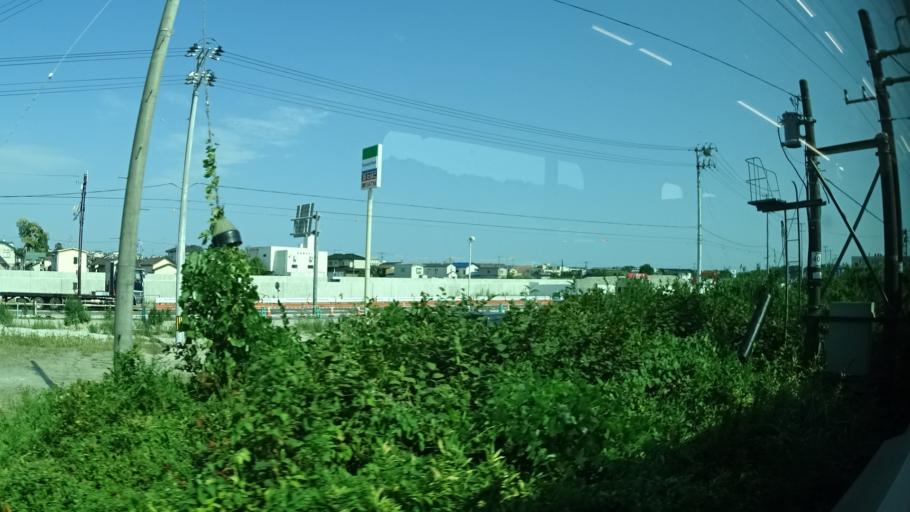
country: JP
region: Miyagi
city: Matsushima
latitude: 38.3832
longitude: 141.0672
